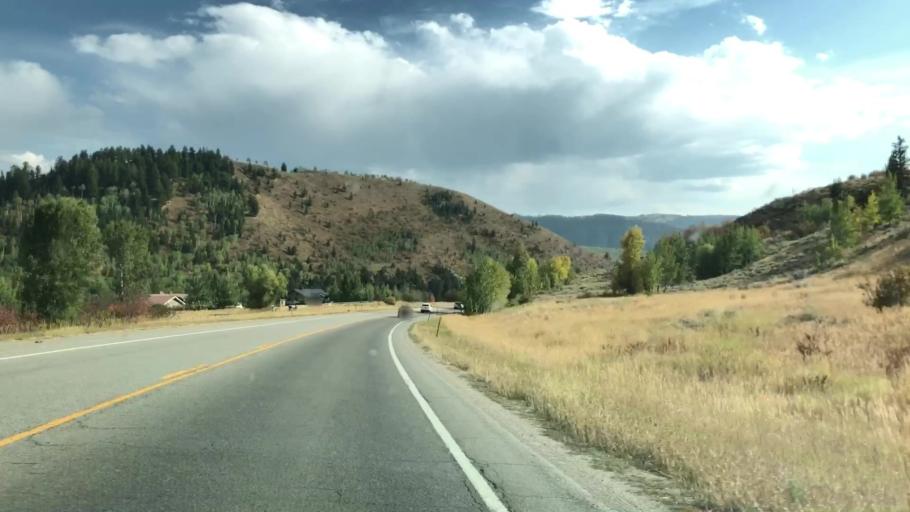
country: US
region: Wyoming
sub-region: Teton County
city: Hoback
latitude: 43.3547
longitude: -110.7206
